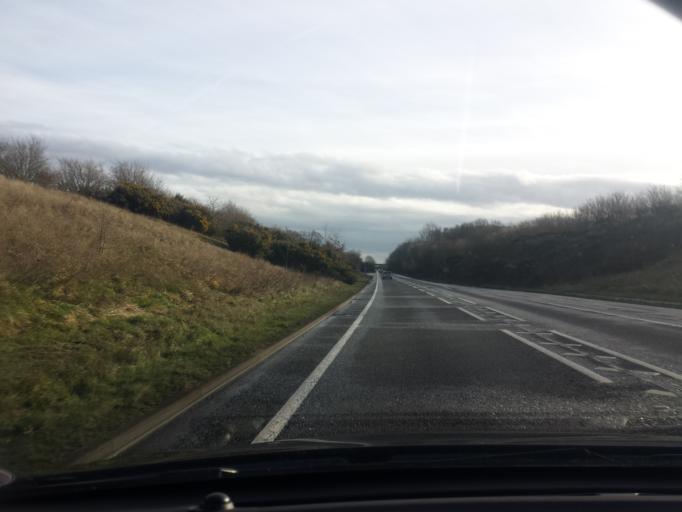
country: GB
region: England
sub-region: Essex
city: Great Bentley
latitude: 51.8468
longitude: 1.1053
